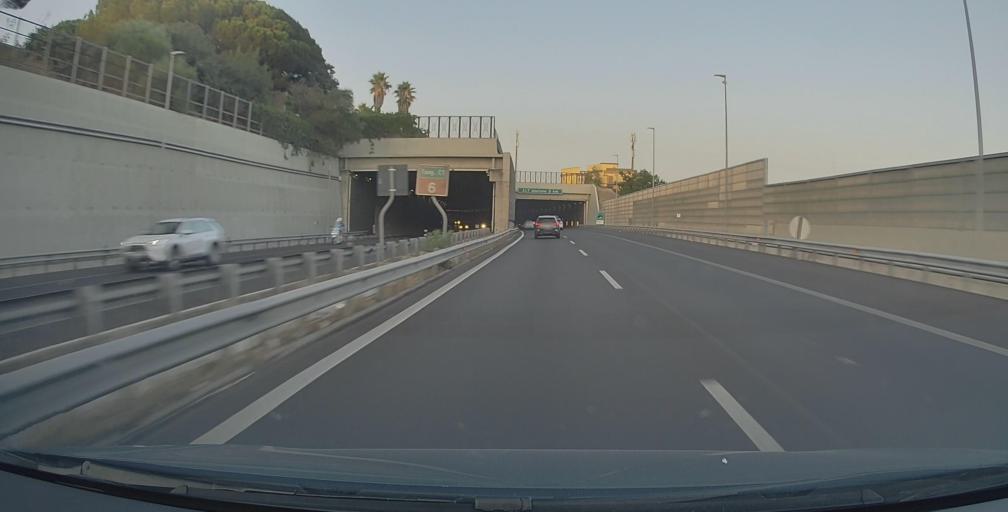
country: IT
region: Sicily
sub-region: Catania
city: Sant'Agata Li Battiati
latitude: 37.5503
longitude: 15.0772
